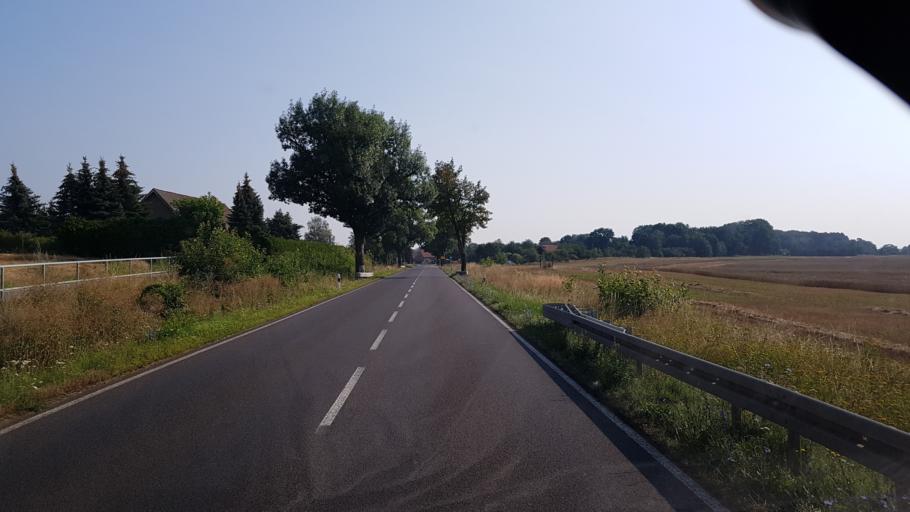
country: DE
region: Brandenburg
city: Kolkwitz
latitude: 51.6957
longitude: 14.2755
